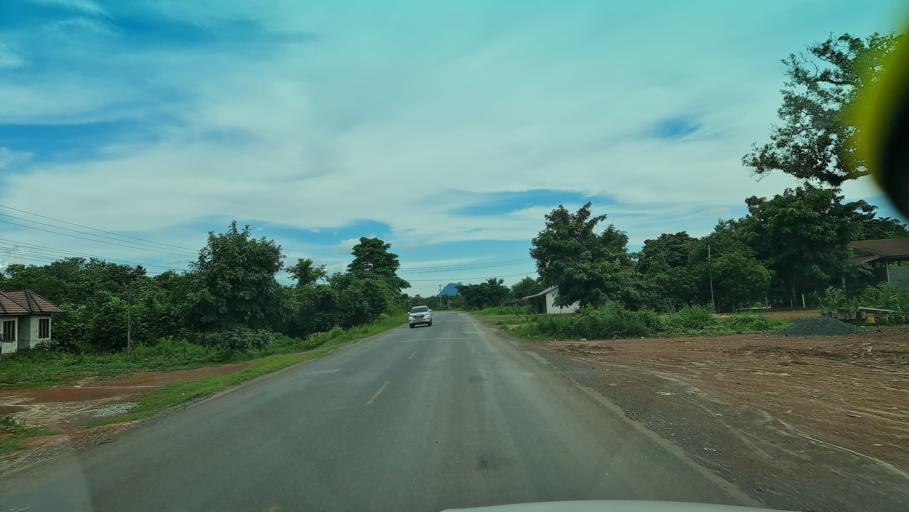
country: LA
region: Bolikhamxai
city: Ban Nahin
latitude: 18.1141
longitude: 104.2737
